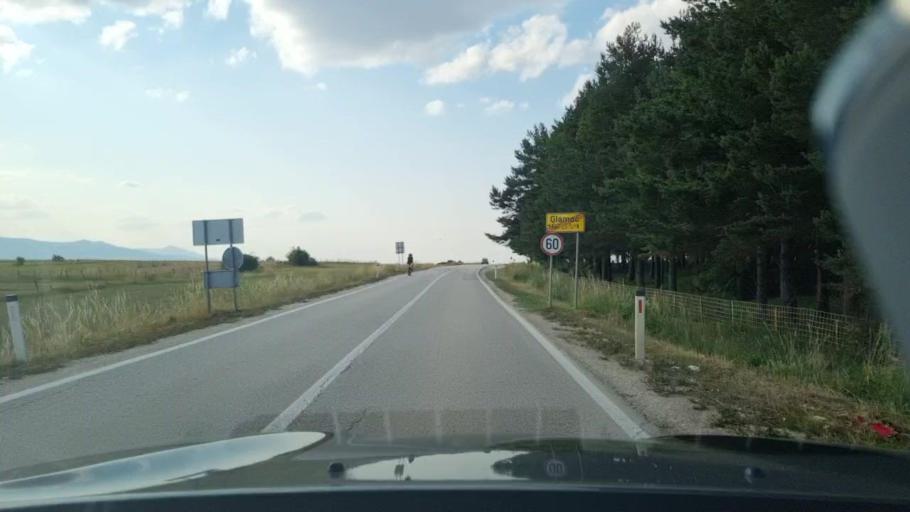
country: BA
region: Federation of Bosnia and Herzegovina
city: Glamoc
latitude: 44.0588
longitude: 16.8282
